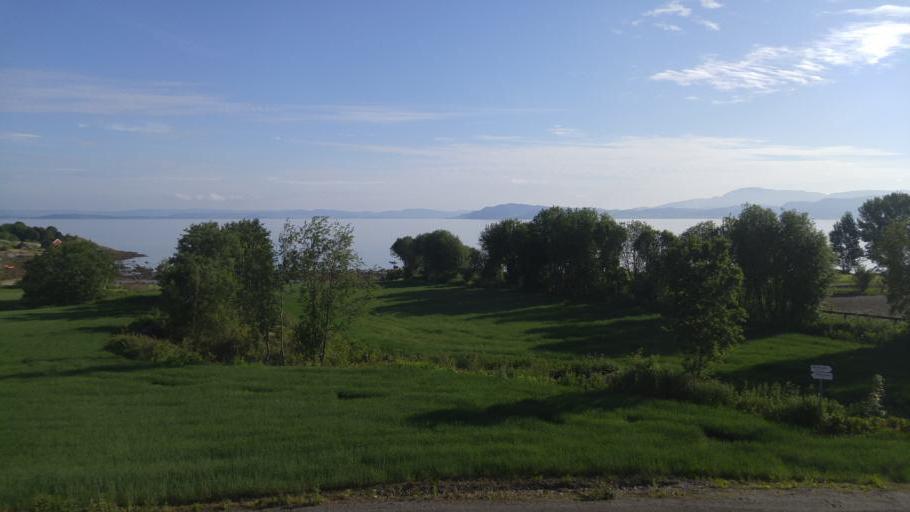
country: NO
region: Sor-Trondelag
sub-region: Malvik
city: Malvik
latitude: 63.4365
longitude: 10.6819
